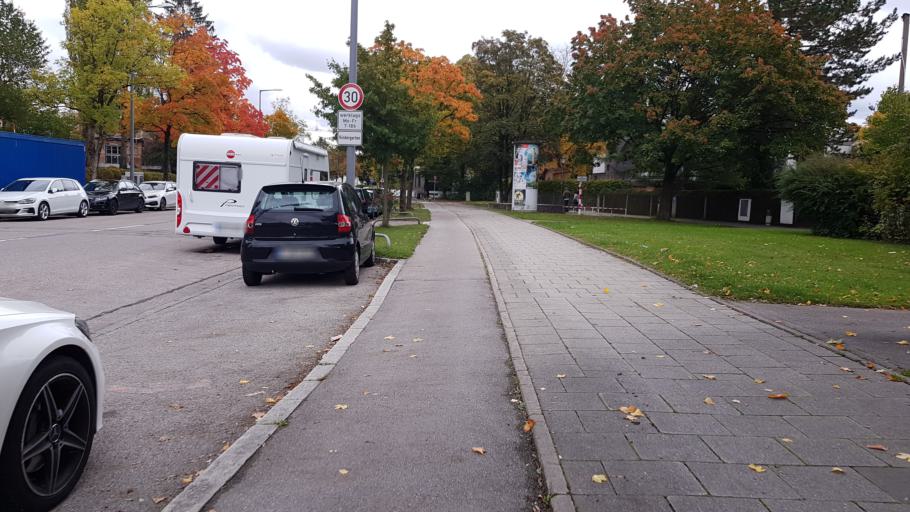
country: DE
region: Bavaria
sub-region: Upper Bavaria
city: Neuried
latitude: 48.1167
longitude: 11.4965
